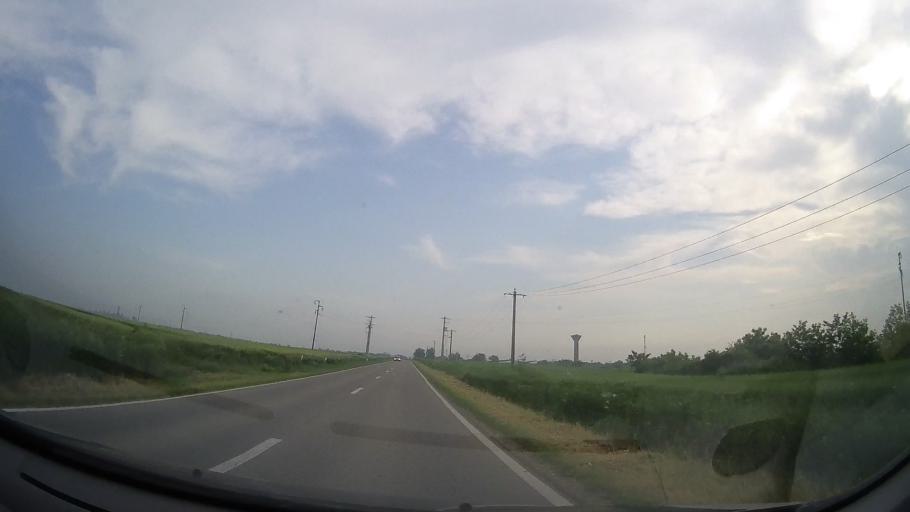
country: RO
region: Timis
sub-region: Comuna Parta
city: Parta
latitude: 45.6504
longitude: 21.1419
